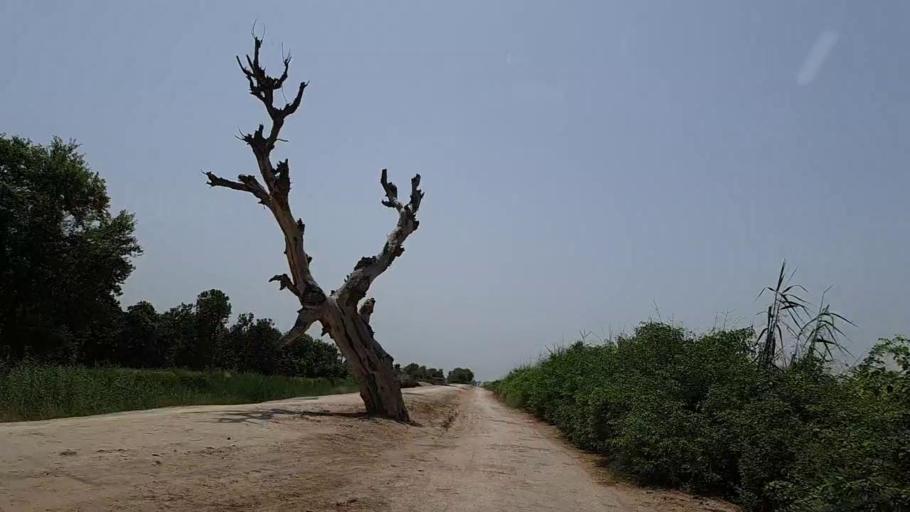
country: PK
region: Sindh
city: Tharu Shah
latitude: 26.9928
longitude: 68.1025
